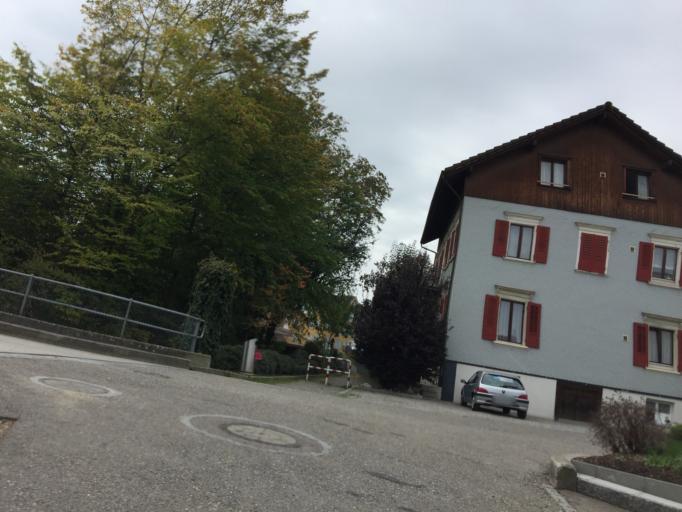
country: CH
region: Saint Gallen
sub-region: Wahlkreis Wil
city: Oberuzwil
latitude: 47.4308
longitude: 9.1240
